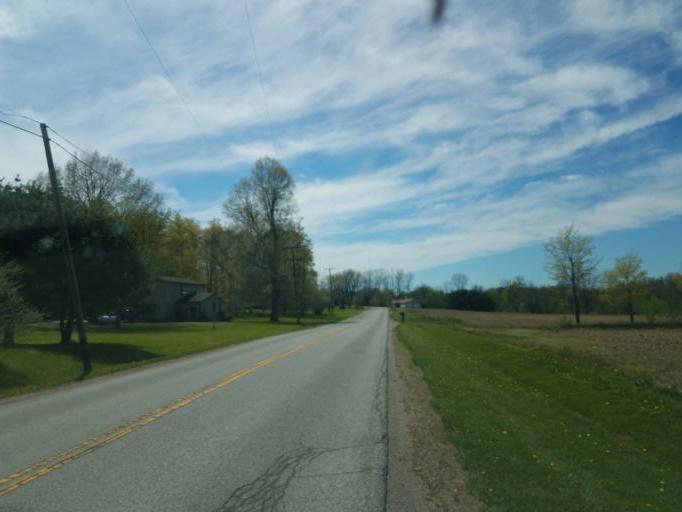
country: US
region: Ohio
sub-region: Ashland County
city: Ashland
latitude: 40.8990
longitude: -82.3361
